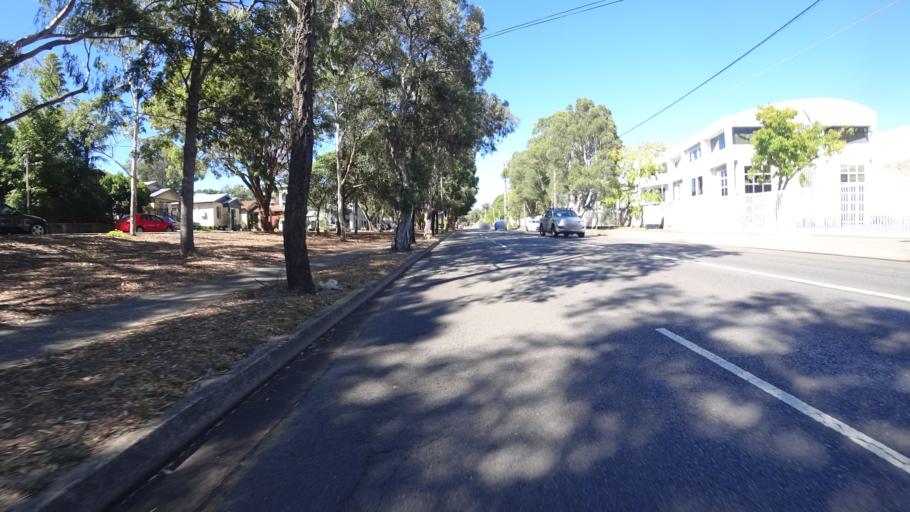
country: AU
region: New South Wales
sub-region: City of Sydney
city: Alexandria
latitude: -33.9086
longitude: 151.2001
